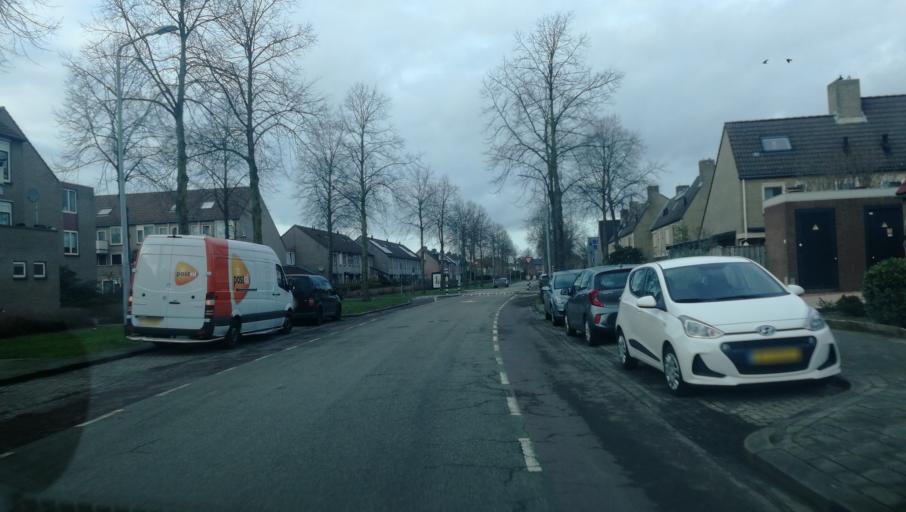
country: NL
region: Limburg
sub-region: Gemeente Venlo
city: Tegelen
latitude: 51.3757
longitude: 6.1275
